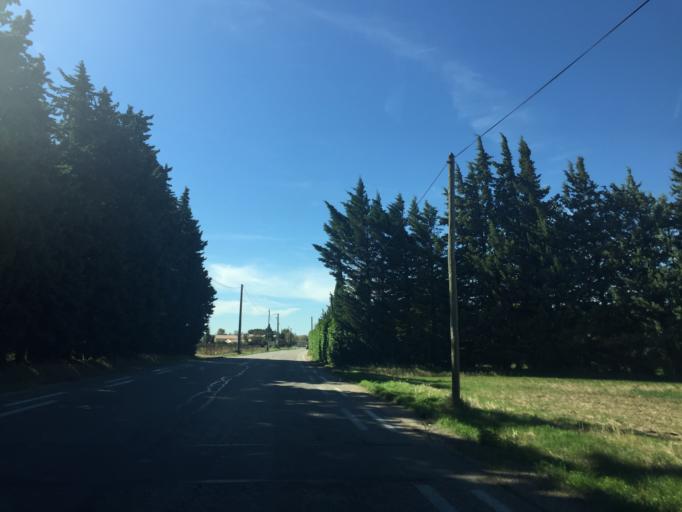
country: FR
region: Provence-Alpes-Cote d'Azur
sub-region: Departement du Vaucluse
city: Caderousse
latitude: 44.1134
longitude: 4.7676
